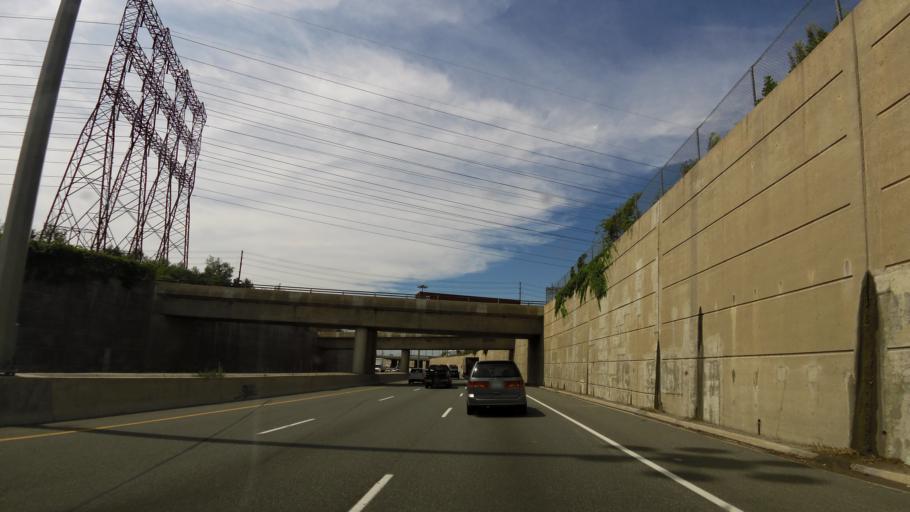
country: CA
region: Ontario
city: Etobicoke
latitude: 43.6986
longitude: -79.5822
